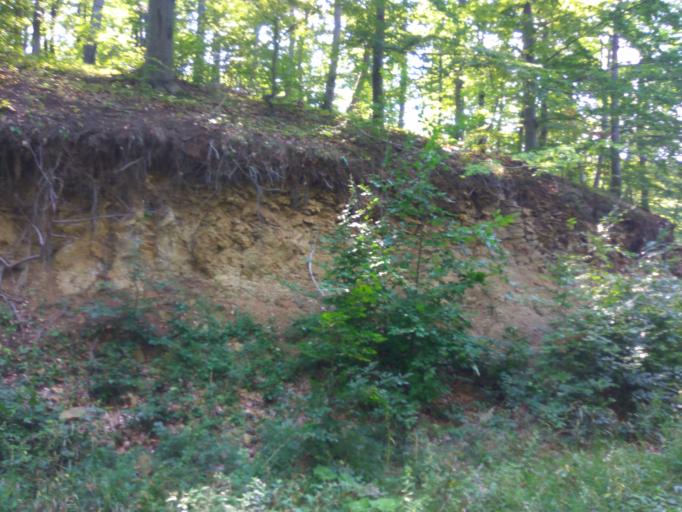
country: HU
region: Heves
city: Paradsasvar
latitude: 47.9063
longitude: 19.9732
